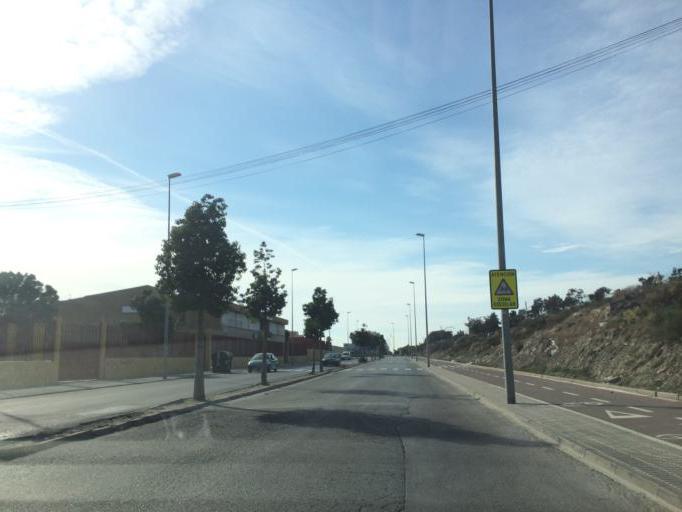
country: ES
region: Andalusia
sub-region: Provincia de Almeria
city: Almeria
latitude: 36.8507
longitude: -2.4324
